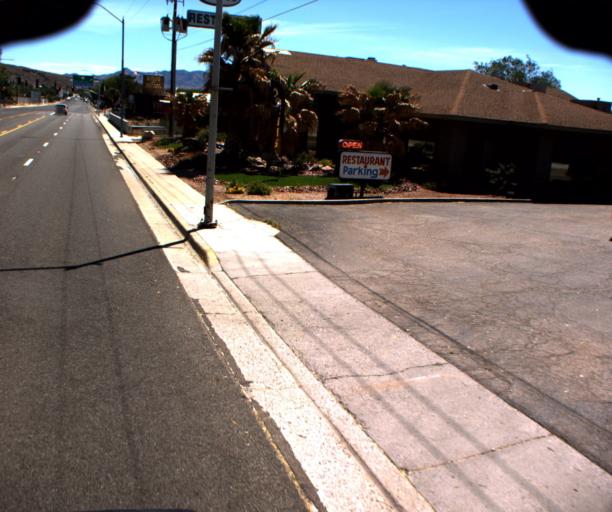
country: US
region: Arizona
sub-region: Mohave County
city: Kingman
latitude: 35.1904
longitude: -114.0630
